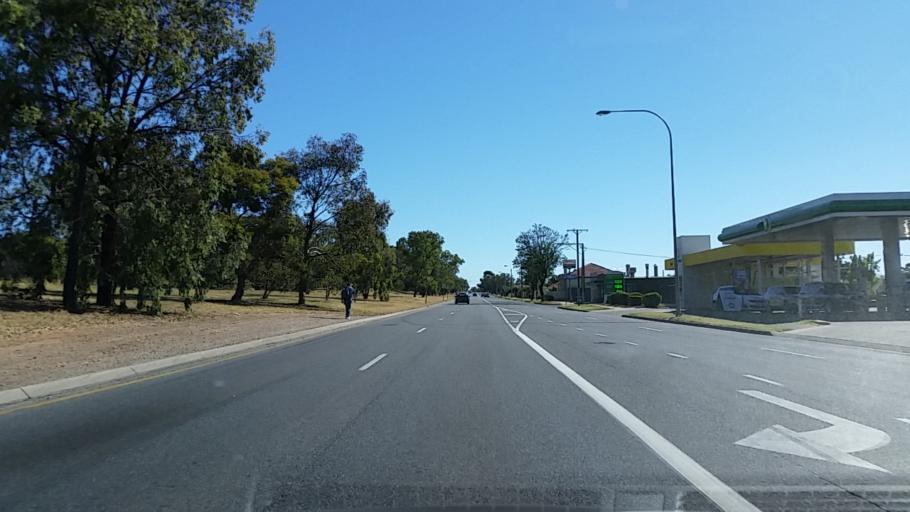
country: AU
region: South Australia
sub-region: Salisbury
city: Ingle Farm
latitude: -34.8281
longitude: 138.6323
